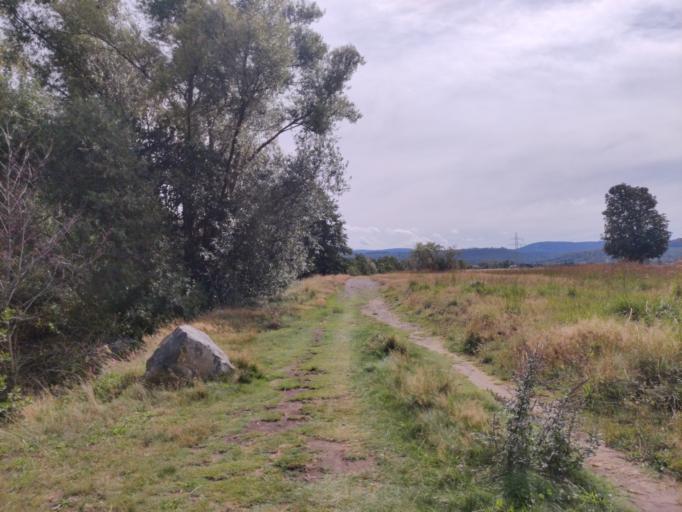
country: DE
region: Lower Saxony
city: Langelsheim
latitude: 51.9535
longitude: 10.3484
